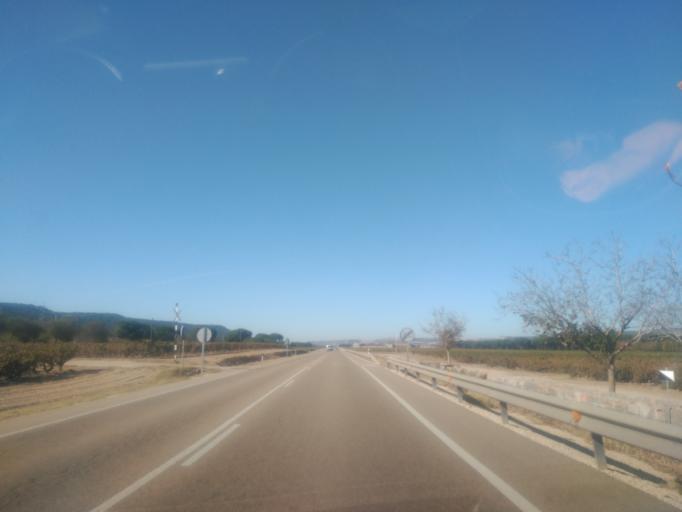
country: ES
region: Castille and Leon
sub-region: Provincia de Valladolid
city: Valbuena de Duero
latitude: 41.6284
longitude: -4.3004
